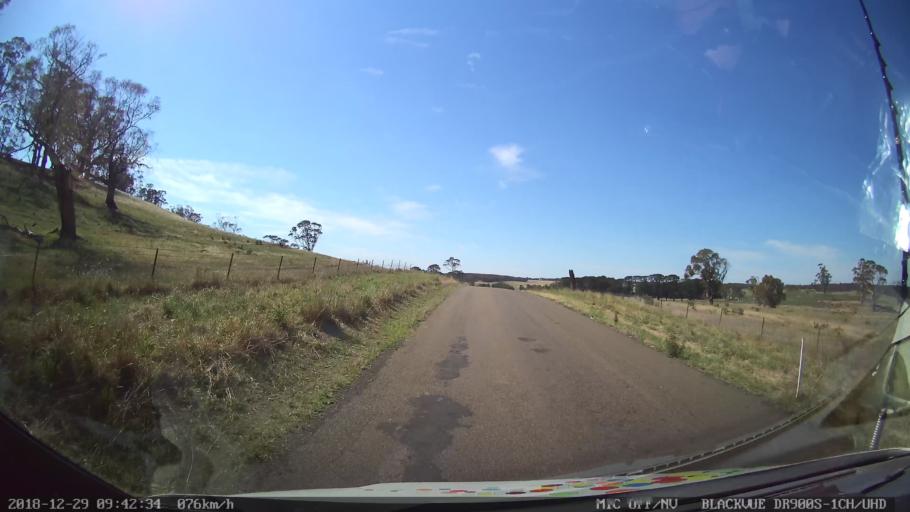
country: AU
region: New South Wales
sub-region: Upper Lachlan Shire
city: Crookwell
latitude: -34.6710
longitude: 149.4211
